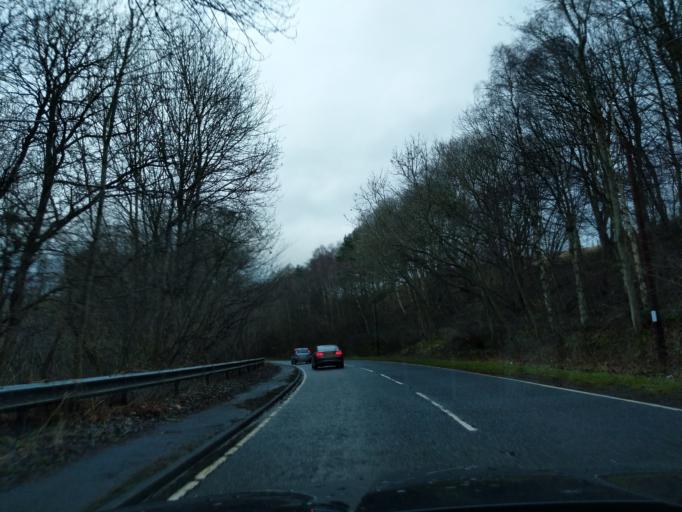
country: GB
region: Scotland
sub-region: The Scottish Borders
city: Galashiels
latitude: 55.6326
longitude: -2.8306
